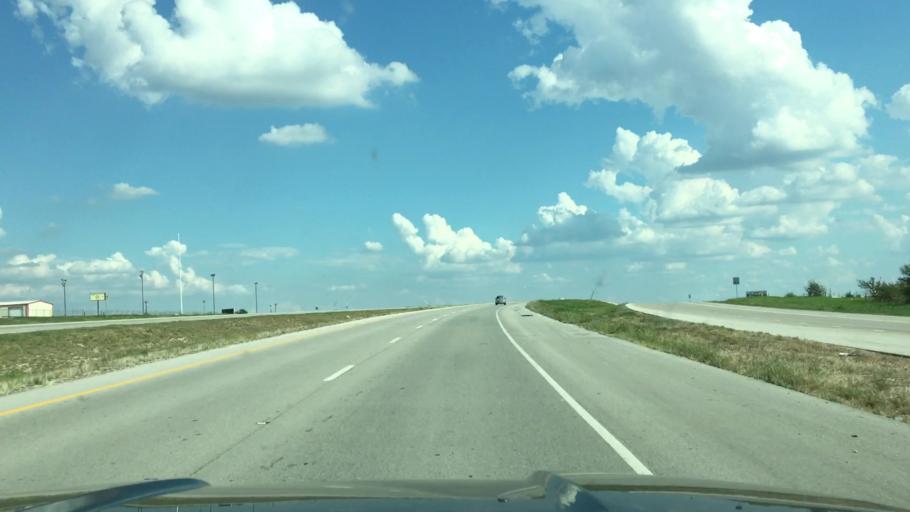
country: US
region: Texas
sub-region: Wise County
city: Decatur
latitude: 33.2071
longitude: -97.5708
